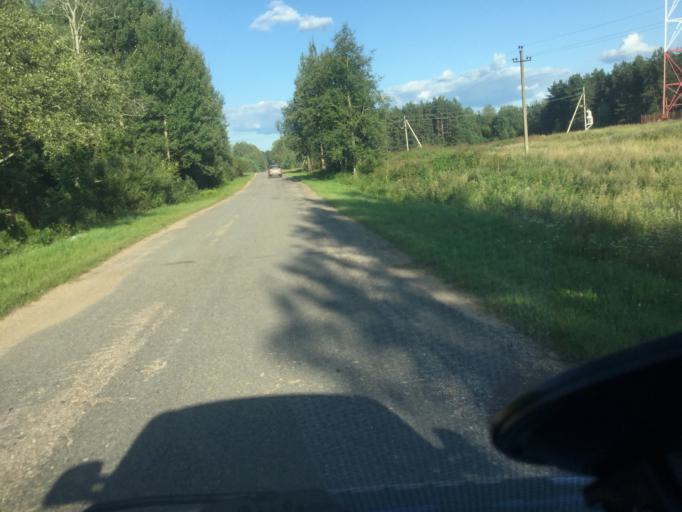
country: BY
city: Osveya
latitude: 56.0214
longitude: 28.2707
